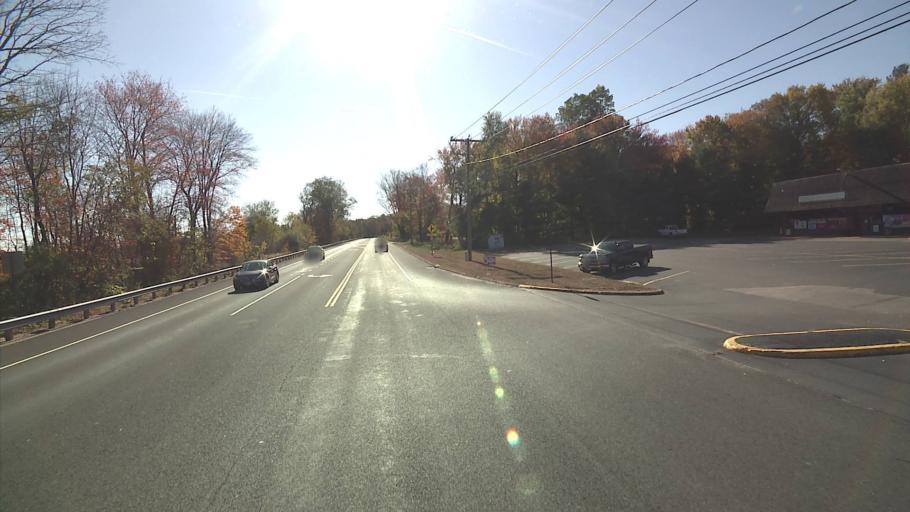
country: US
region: Connecticut
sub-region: Tolland County
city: Coventry Lake
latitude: 41.7523
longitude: -72.3974
